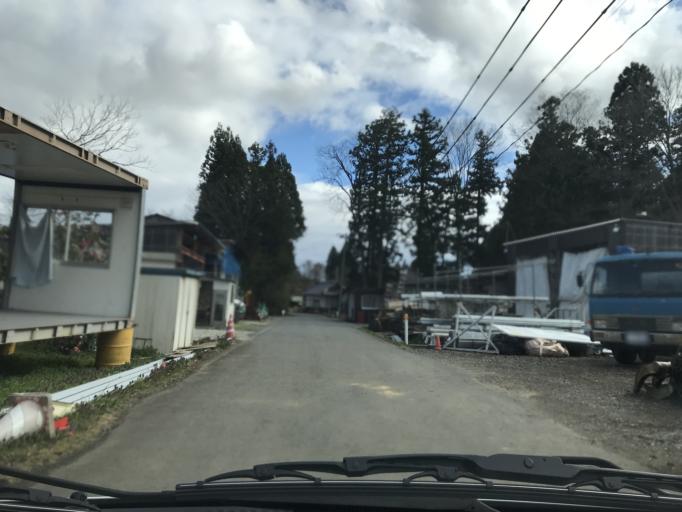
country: JP
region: Iwate
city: Mizusawa
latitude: 39.1054
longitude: 141.0791
